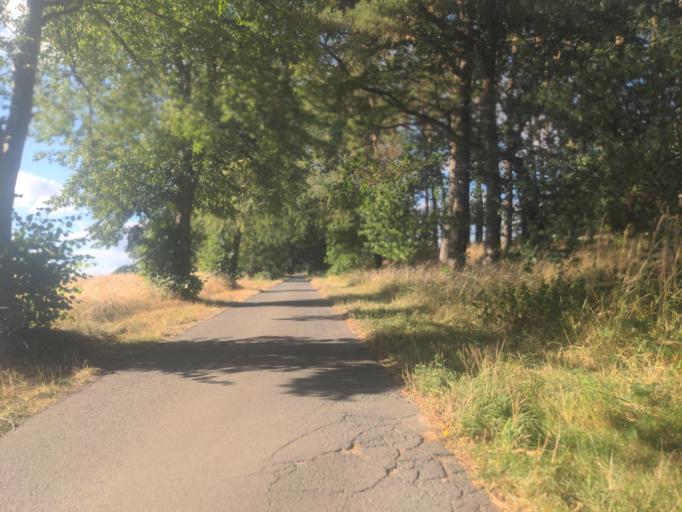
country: DE
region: Lower Saxony
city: Tosterglope
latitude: 53.2019
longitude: 10.8241
